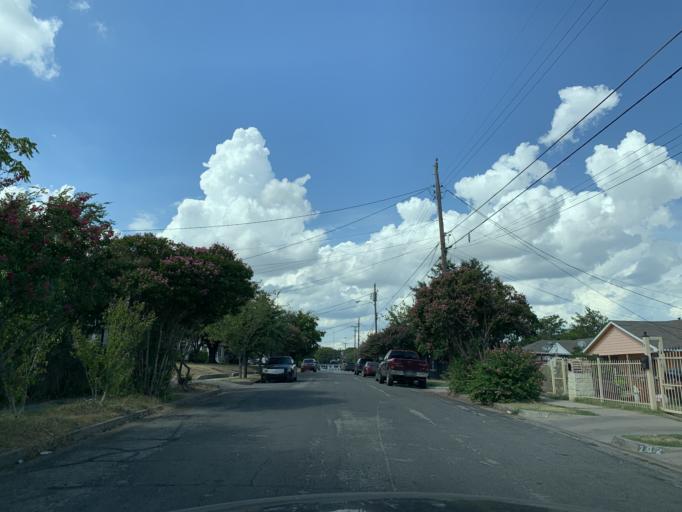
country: US
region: Texas
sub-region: Dallas County
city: Cockrell Hill
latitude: 32.7466
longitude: -96.8688
